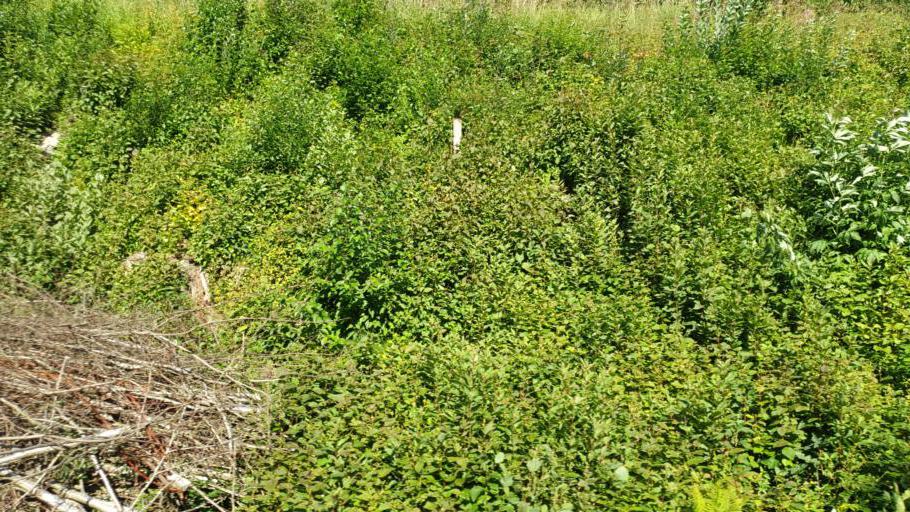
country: NO
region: Sor-Trondelag
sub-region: Orkdal
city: Orkanger
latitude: 63.1992
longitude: 9.7845
